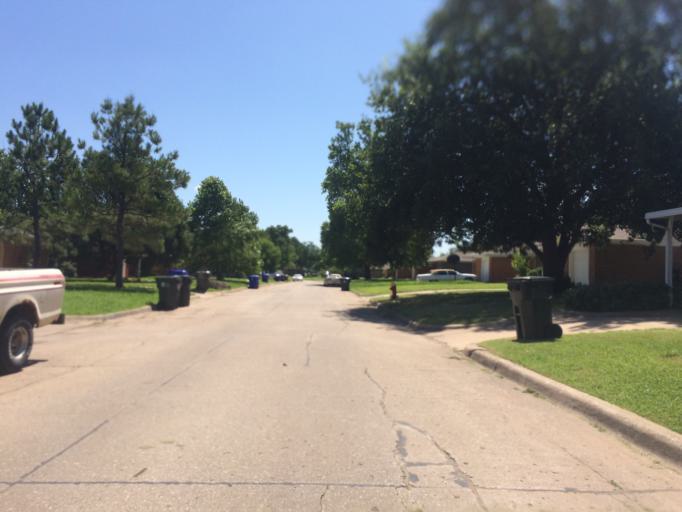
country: US
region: Oklahoma
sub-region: Cleveland County
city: Norman
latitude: 35.2371
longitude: -97.4469
